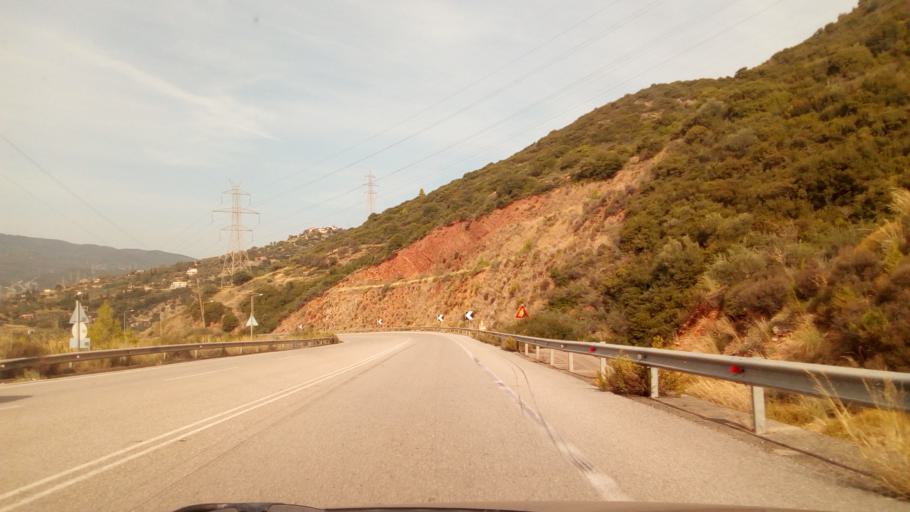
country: GR
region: West Greece
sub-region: Nomos Aitolias kai Akarnanias
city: Nafpaktos
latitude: 38.4003
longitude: 21.8157
